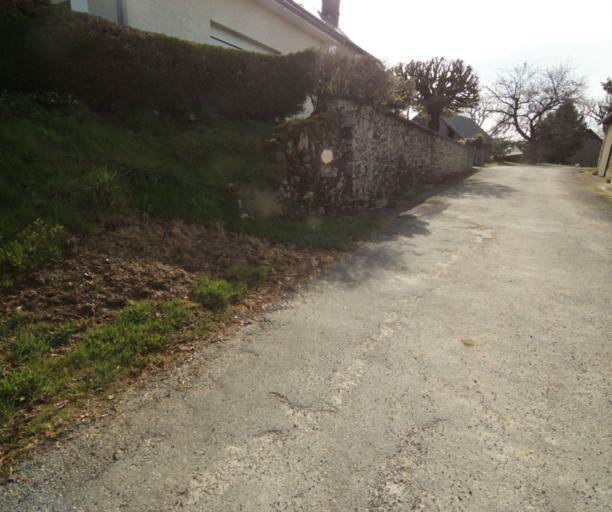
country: FR
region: Limousin
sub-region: Departement de la Correze
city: Correze
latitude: 45.3389
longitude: 1.8629
